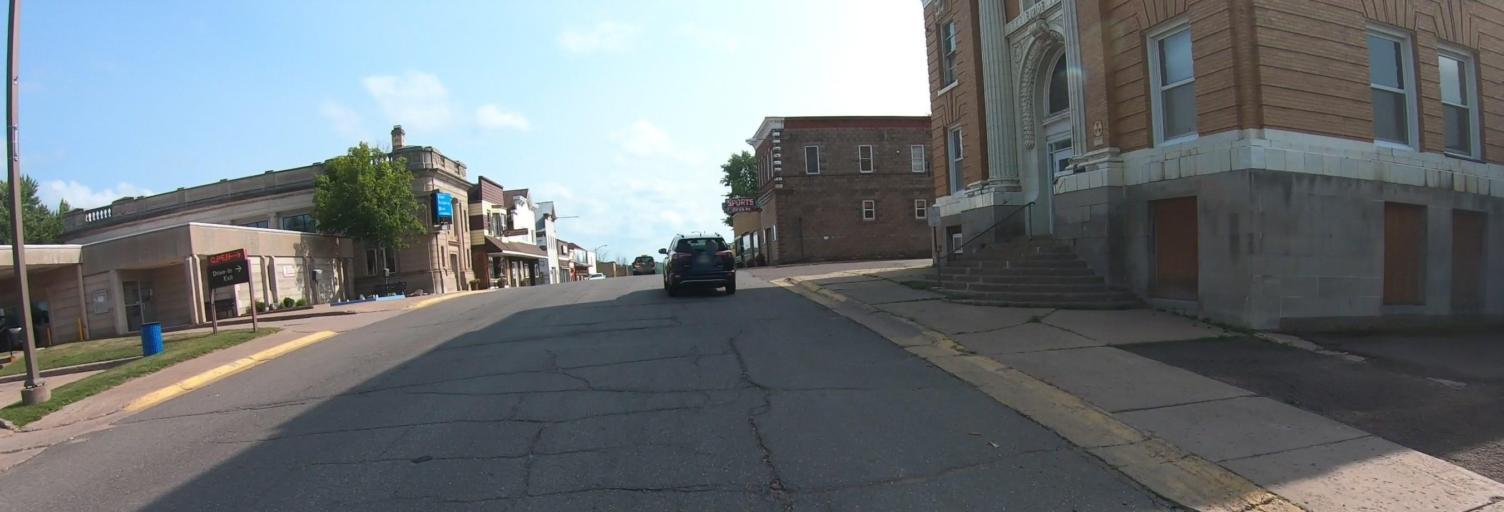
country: US
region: Michigan
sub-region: Gogebic County
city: Wakefield
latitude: 46.4750
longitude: -89.9411
